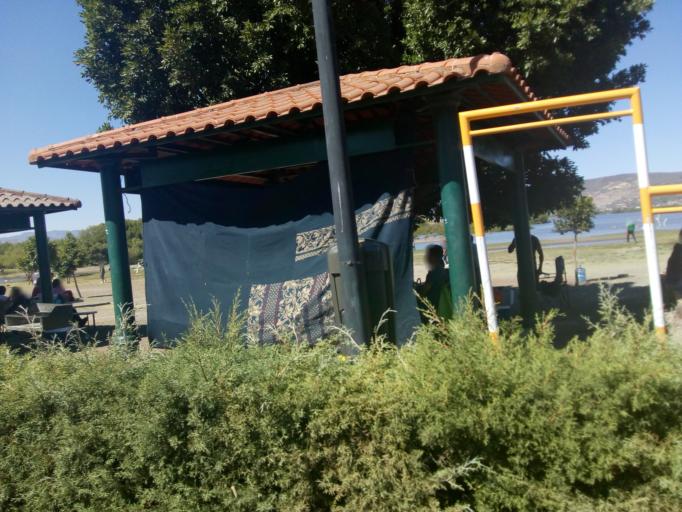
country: MX
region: Guanajuato
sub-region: Leon
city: La Ermita
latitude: 21.1744
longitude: -101.6978
